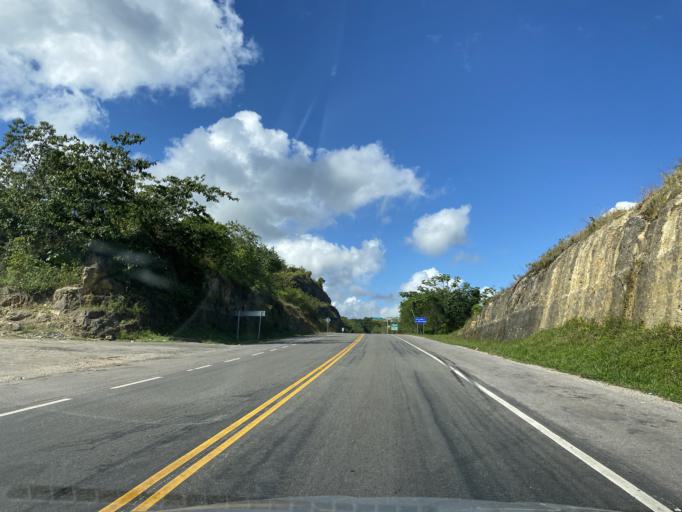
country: DO
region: Monte Plata
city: Majagual
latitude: 19.0423
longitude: -69.8297
